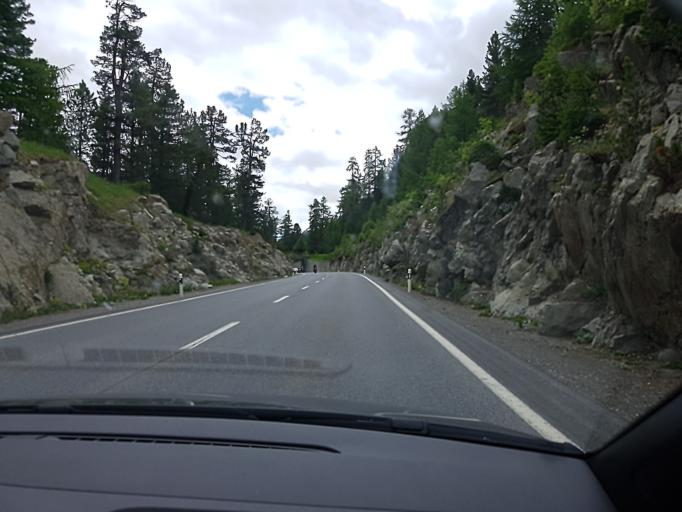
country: CH
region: Grisons
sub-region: Maloja District
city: Pontresina
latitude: 46.4888
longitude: 9.9038
